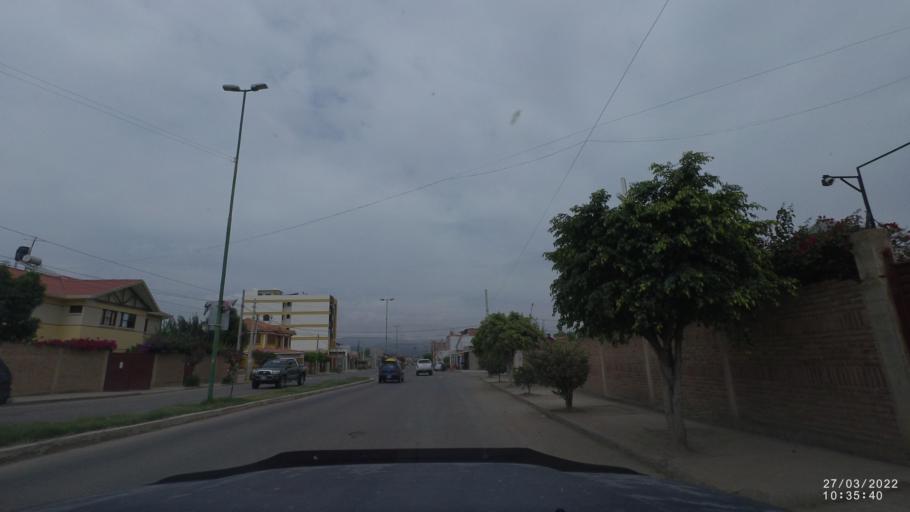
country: BO
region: Cochabamba
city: Cochabamba
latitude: -17.4398
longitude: -66.1493
